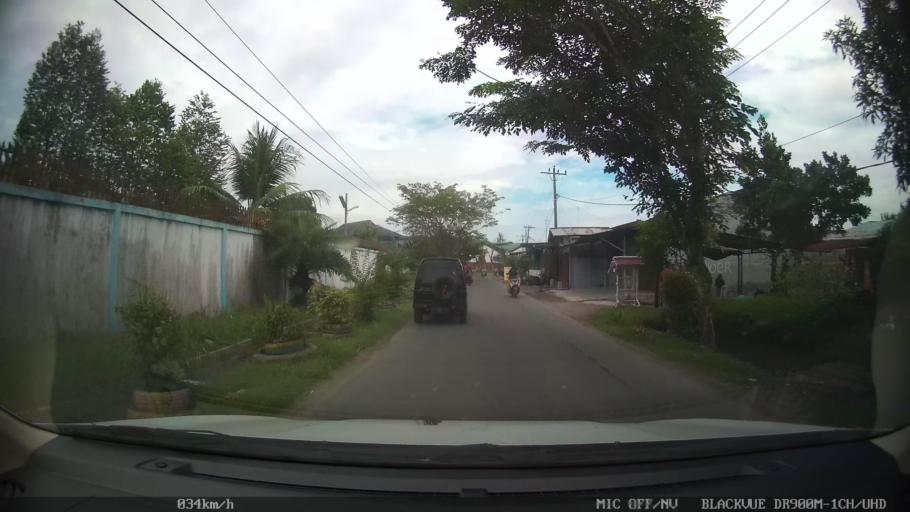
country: ID
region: North Sumatra
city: Sunggal
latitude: 3.6231
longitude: 98.5945
